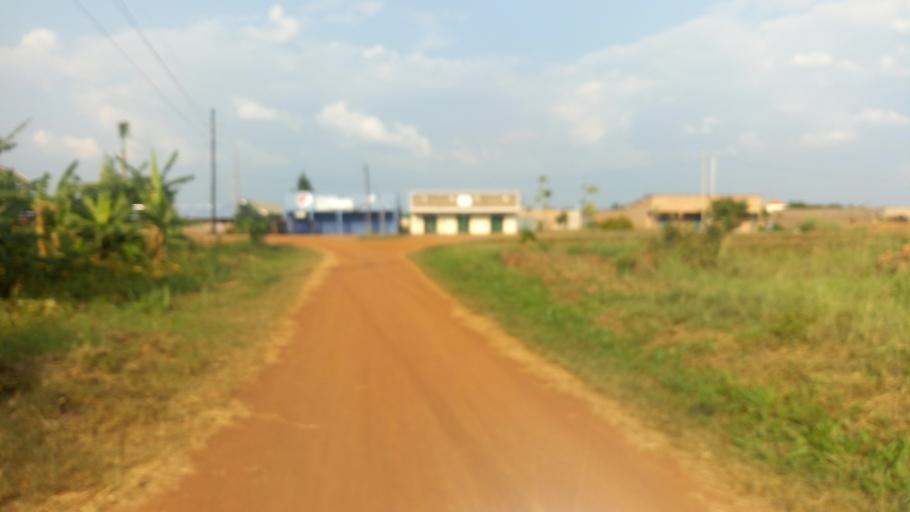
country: UG
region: Western Region
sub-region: Kiryandongo District
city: Kiryandongo
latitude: 1.8056
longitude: 32.0093
